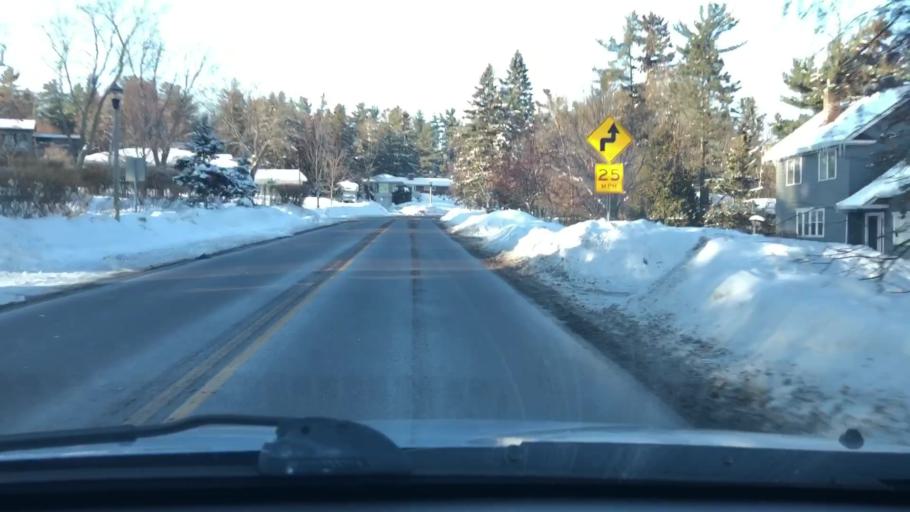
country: US
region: Minnesota
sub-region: Saint Louis County
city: Duluth
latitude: 46.8180
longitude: -92.0700
